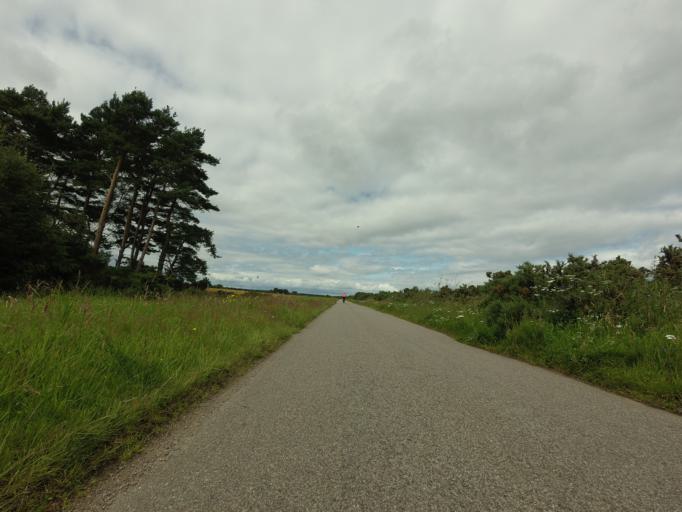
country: GB
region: Scotland
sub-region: Moray
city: Kinloss
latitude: 57.6287
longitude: -3.5948
